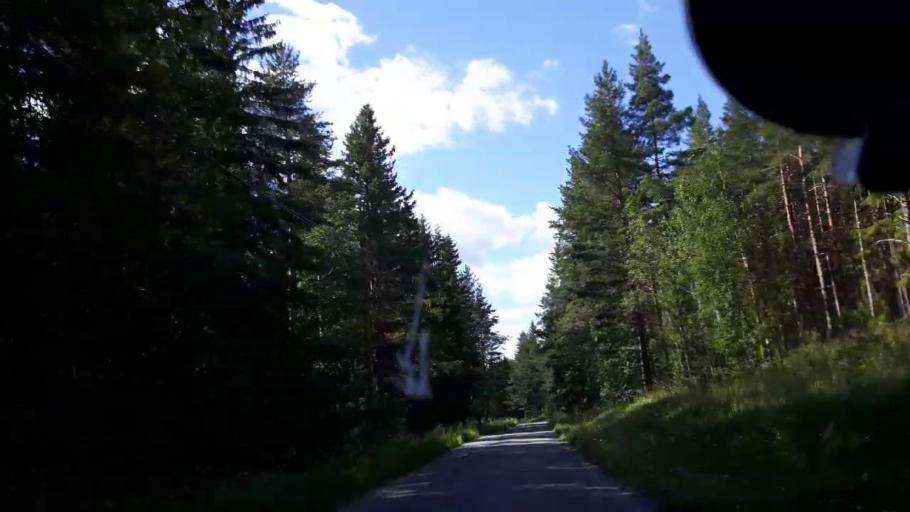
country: SE
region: Jaemtland
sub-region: Braecke Kommun
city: Braecke
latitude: 62.8570
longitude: 15.2825
